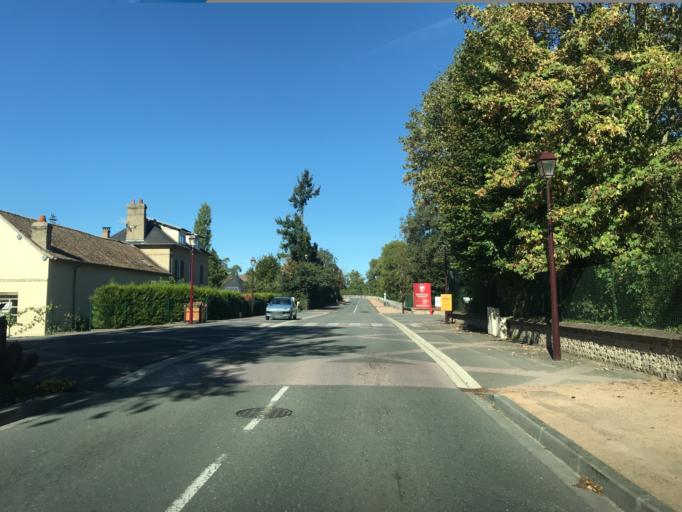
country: FR
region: Haute-Normandie
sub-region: Departement de l'Eure
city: Le Vaudreuil
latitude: 49.2534
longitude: 1.2090
